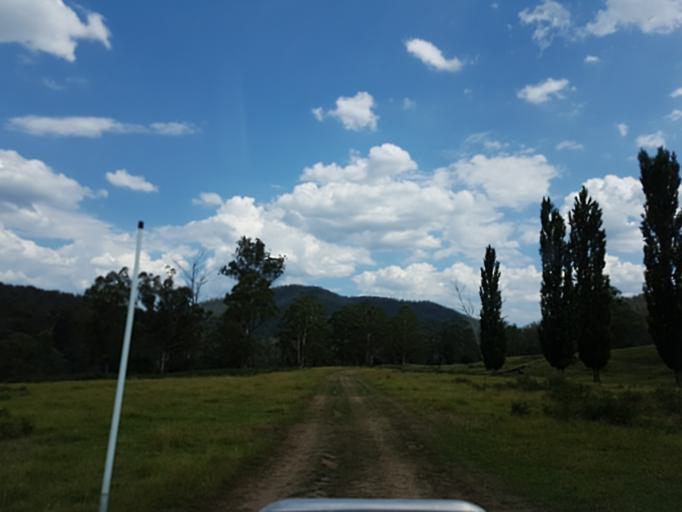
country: AU
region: Victoria
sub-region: East Gippsland
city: Lakes Entrance
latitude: -37.4015
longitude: 148.3337
